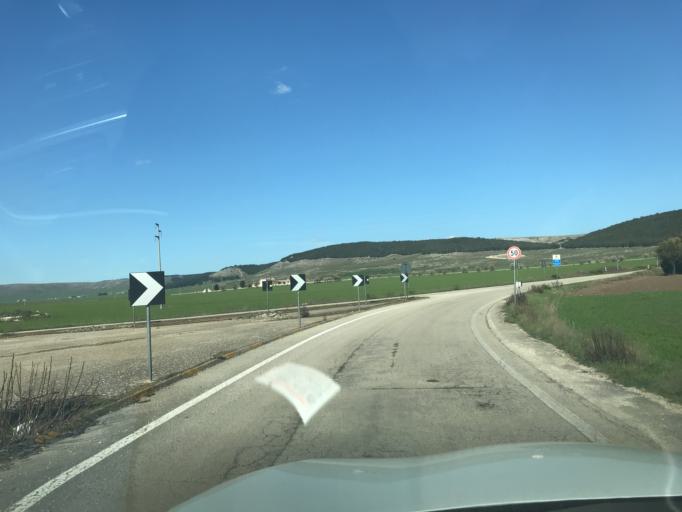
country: IT
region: Apulia
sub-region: Provincia di Bari
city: Gravina in Puglia
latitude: 40.8612
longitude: 16.4370
